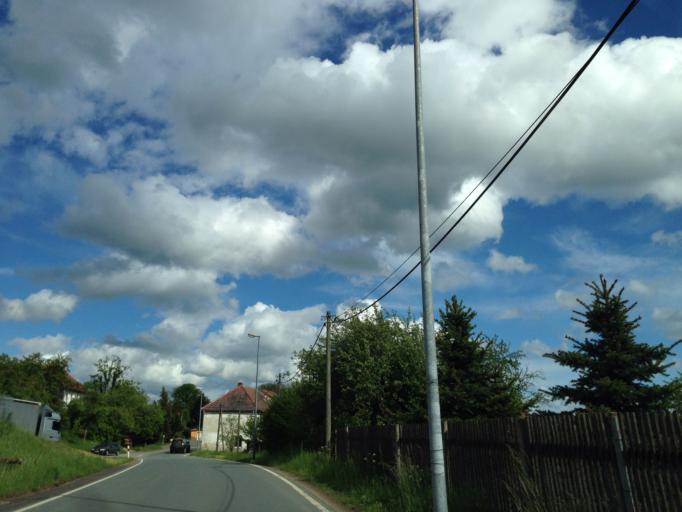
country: DE
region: Thuringia
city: Reinstadt
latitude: 50.7726
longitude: 11.4597
